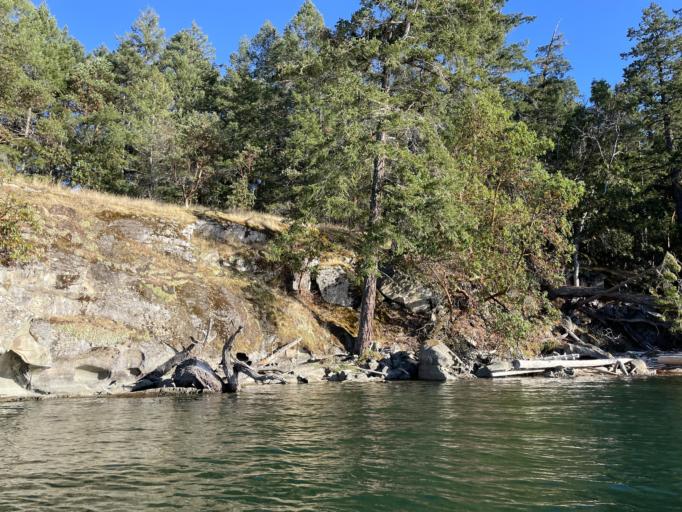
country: CA
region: British Columbia
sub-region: Cowichan Valley Regional District
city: Ladysmith
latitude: 49.0983
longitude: -123.7288
